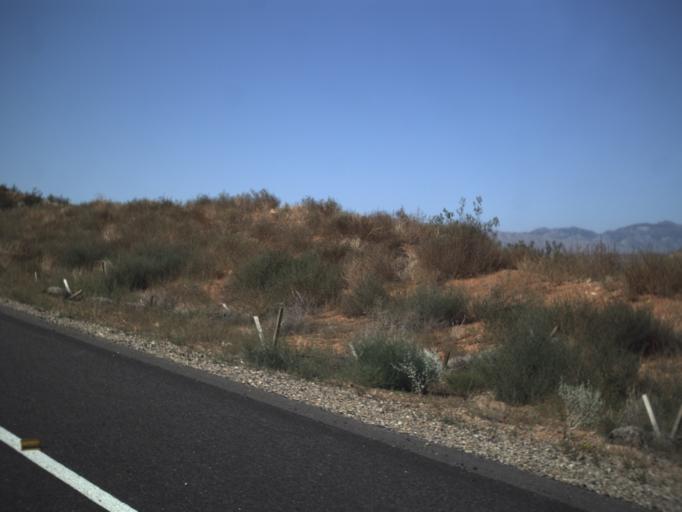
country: US
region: Utah
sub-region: Washington County
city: Washington
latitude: 37.1127
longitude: -113.4581
